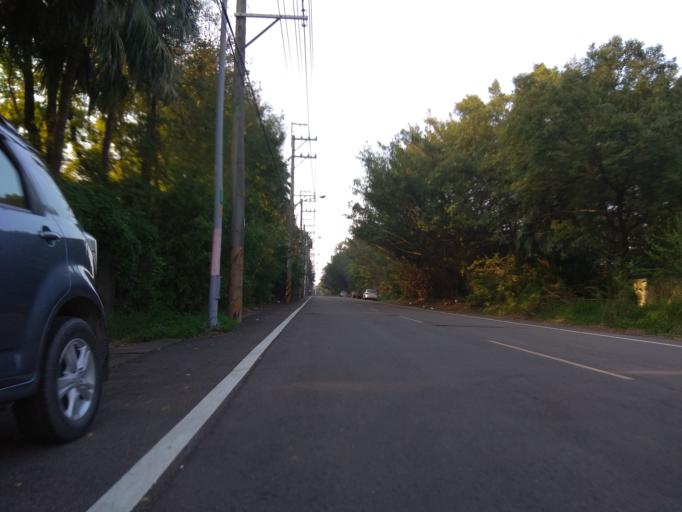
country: TW
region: Taiwan
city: Daxi
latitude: 24.9255
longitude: 121.1821
